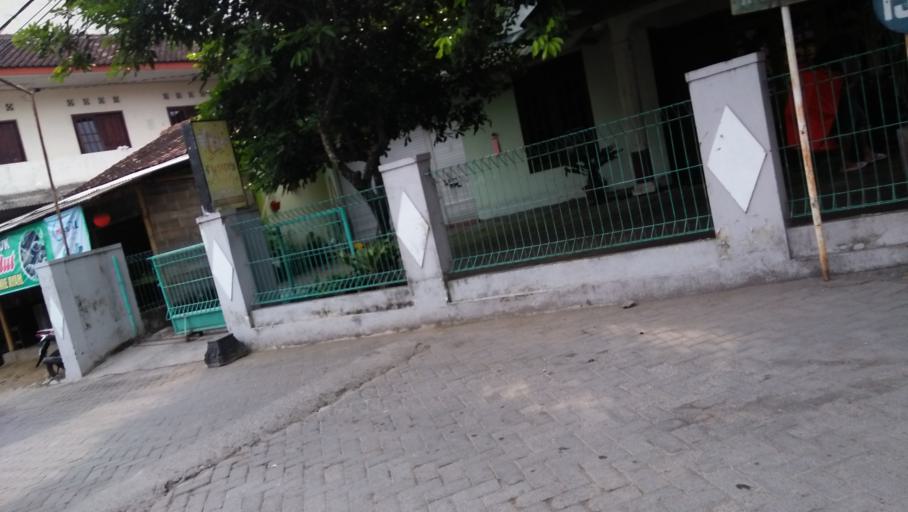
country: ID
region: Daerah Istimewa Yogyakarta
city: Yogyakarta
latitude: -7.7643
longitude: 110.3873
